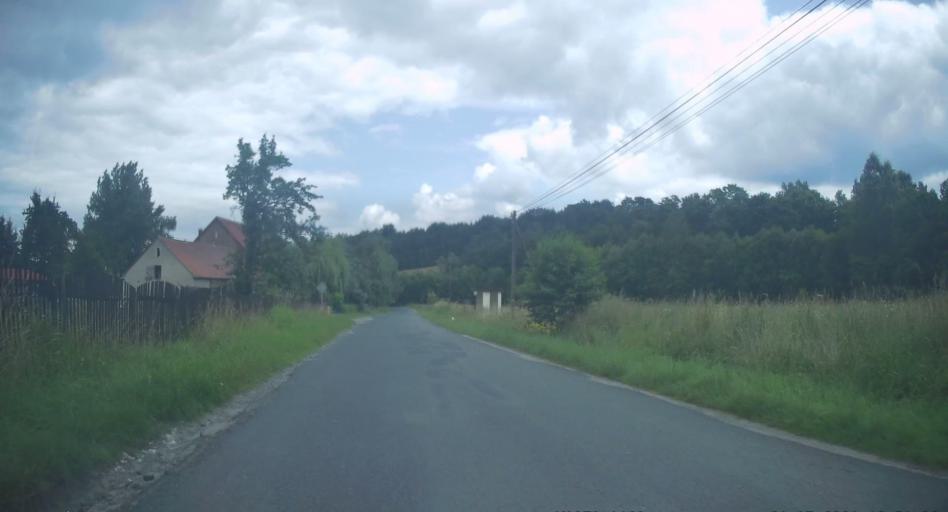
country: PL
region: Lower Silesian Voivodeship
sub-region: Powiat kamiennogorski
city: Marciszow
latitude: 50.8395
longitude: 15.9788
